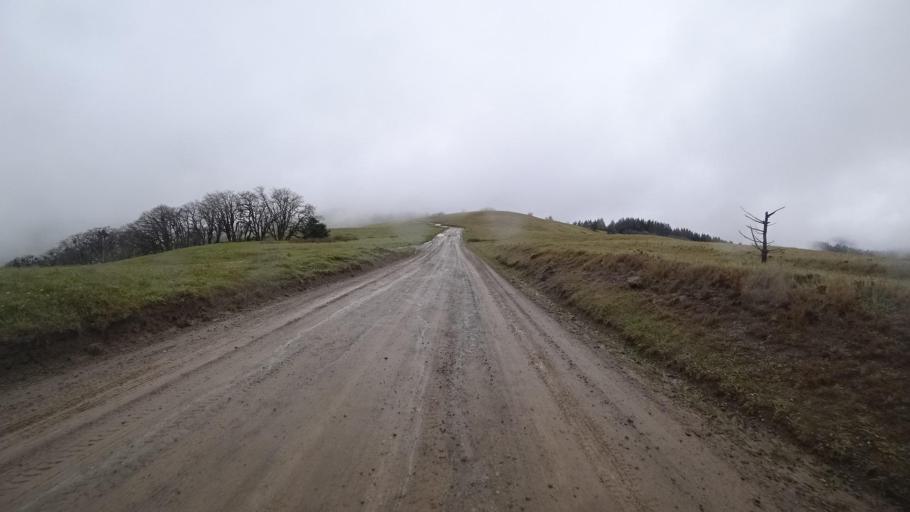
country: US
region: California
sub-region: Humboldt County
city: Westhaven-Moonstone
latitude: 41.1431
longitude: -123.8657
